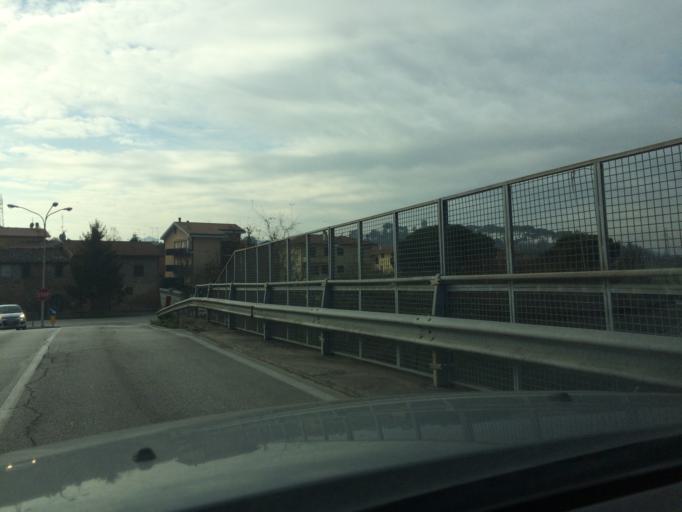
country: IT
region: Umbria
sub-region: Provincia di Perugia
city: Via Lippia
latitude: 43.0875
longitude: 12.4807
